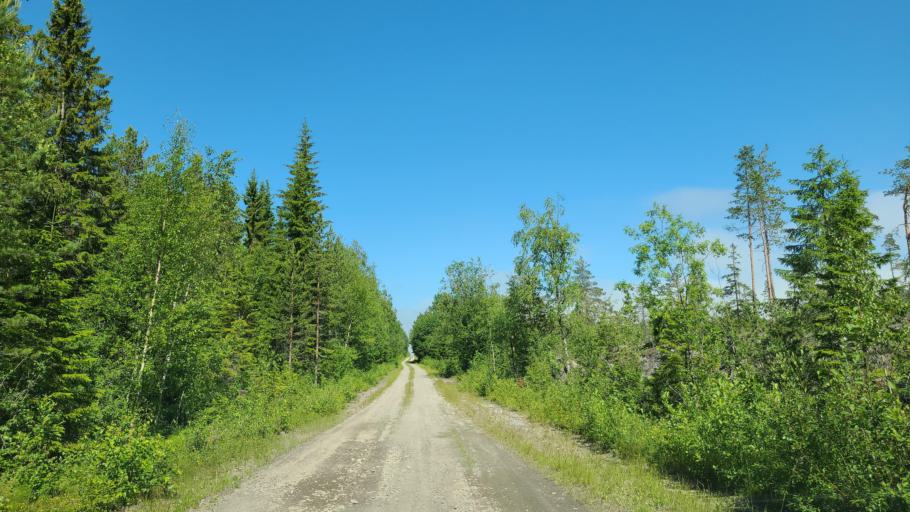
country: SE
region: Vaesternorrland
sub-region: OErnskoeldsviks Kommun
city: Husum
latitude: 63.4341
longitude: 19.2303
